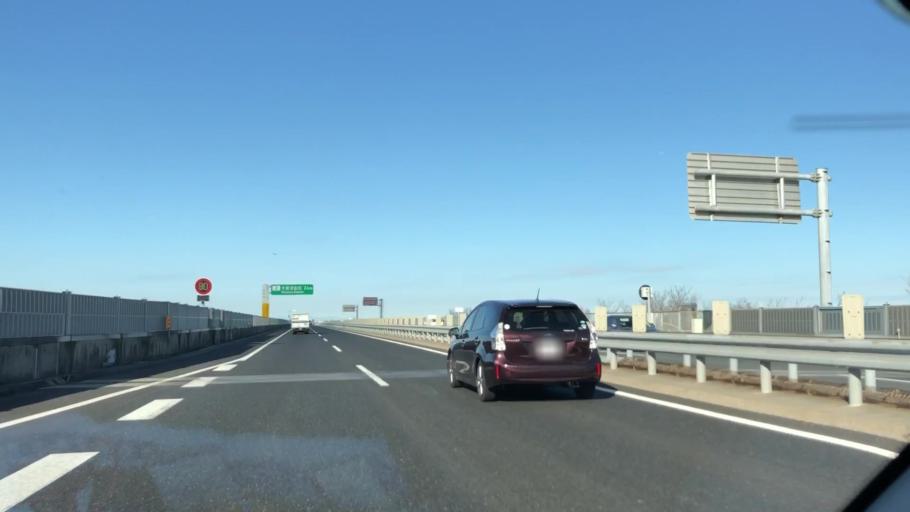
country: JP
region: Chiba
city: Kisarazu
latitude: 35.4163
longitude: 139.9481
